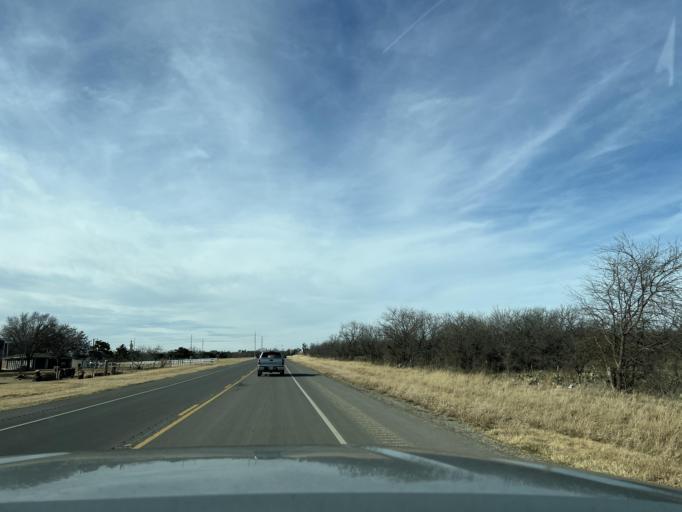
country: US
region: Texas
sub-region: Shackelford County
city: Albany
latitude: 32.7192
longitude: -99.2884
